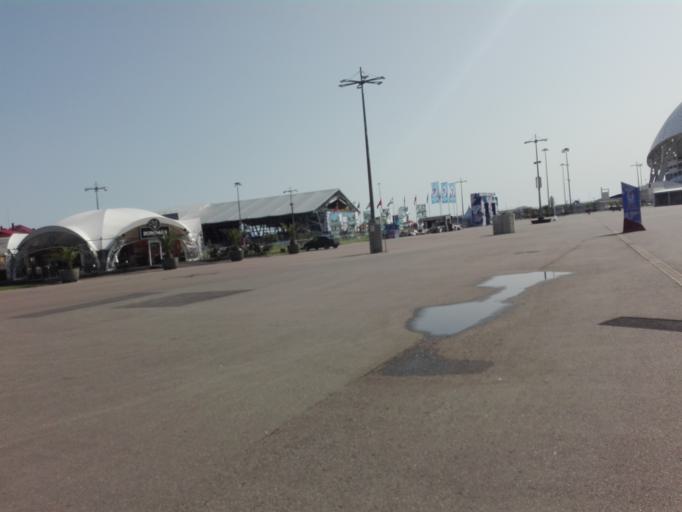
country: RU
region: Krasnodarskiy
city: Adler
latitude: 43.4048
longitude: 39.9584
